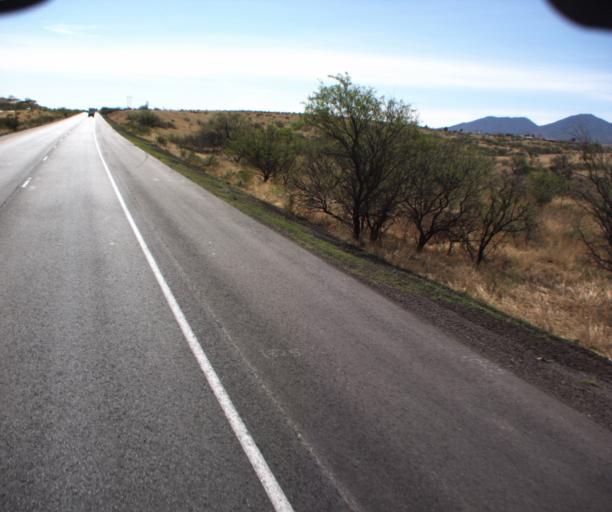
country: US
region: Arizona
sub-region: Cochise County
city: Mescal
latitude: 31.9671
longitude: -110.4659
